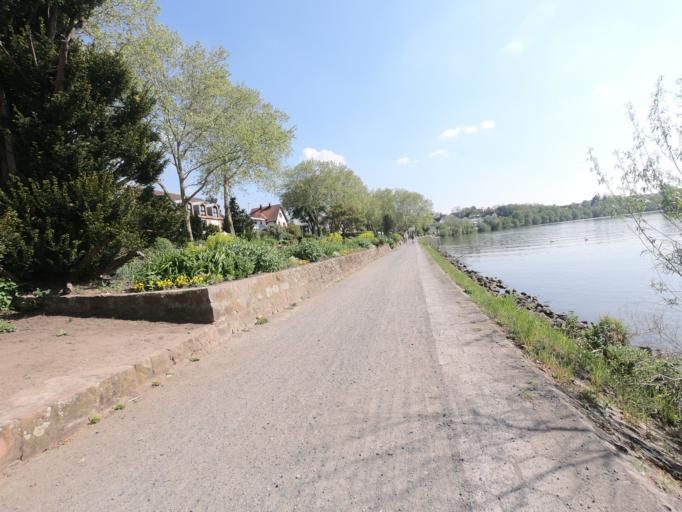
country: DE
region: Hesse
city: Kelsterbach
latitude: 50.0687
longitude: 8.5281
